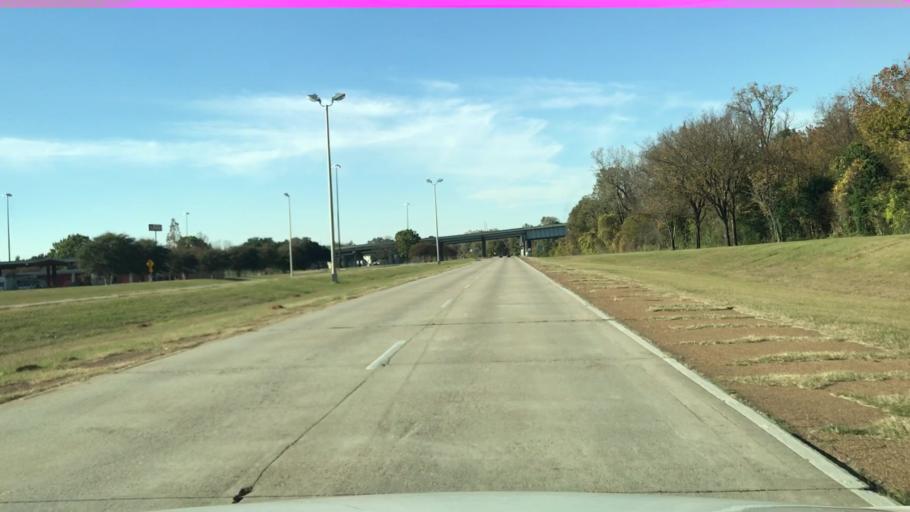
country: US
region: Louisiana
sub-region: Bossier Parish
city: Bossier City
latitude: 32.4883
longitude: -93.6980
